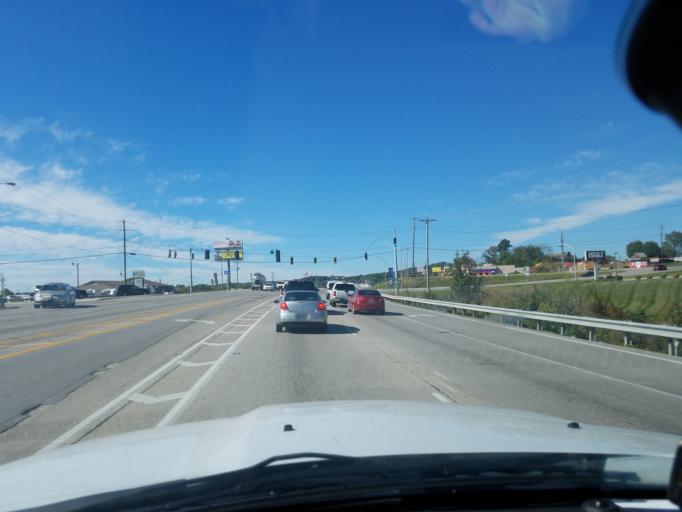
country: US
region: Kentucky
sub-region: Laurel County
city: London
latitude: 37.1059
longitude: -84.0839
